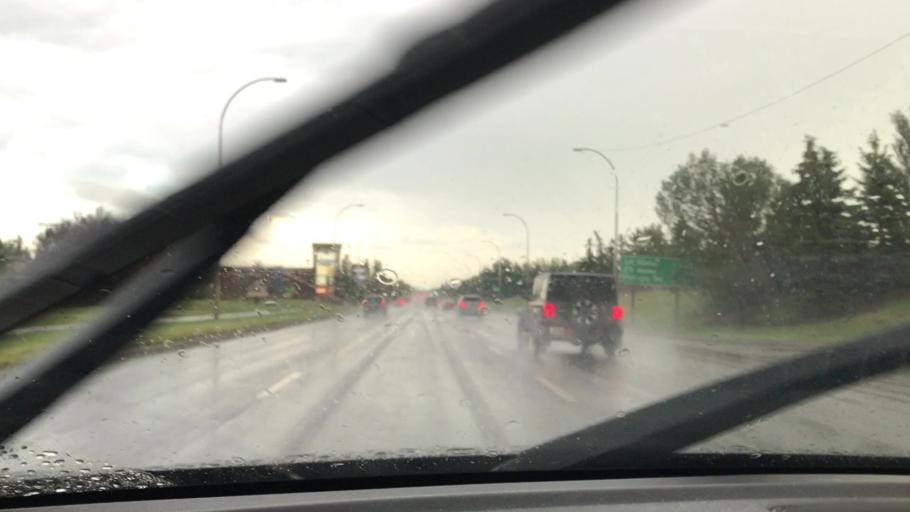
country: CA
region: Alberta
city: Edmonton
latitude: 53.4773
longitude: -113.4956
